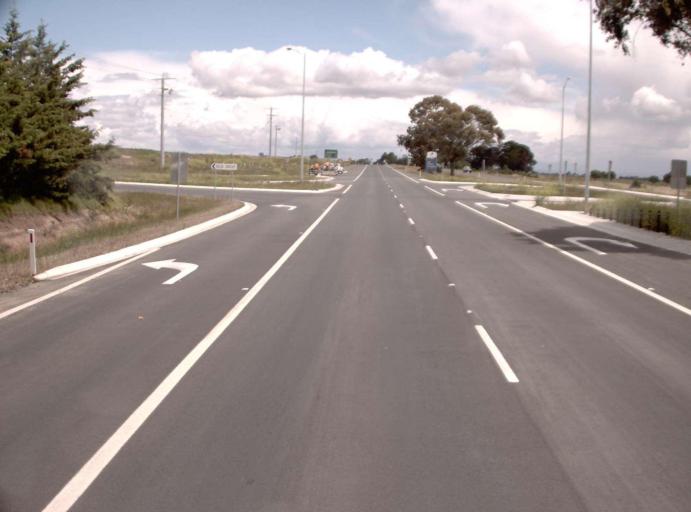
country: AU
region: Victoria
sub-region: Wellington
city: Sale
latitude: -38.1038
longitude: 147.0227
